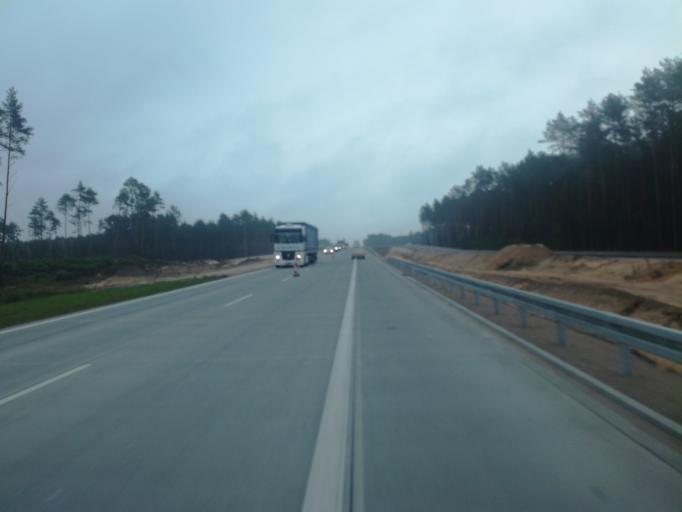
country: PL
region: Masovian Voivodeship
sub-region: Powiat ostrowski
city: Brok
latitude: 52.7328
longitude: 21.7398
